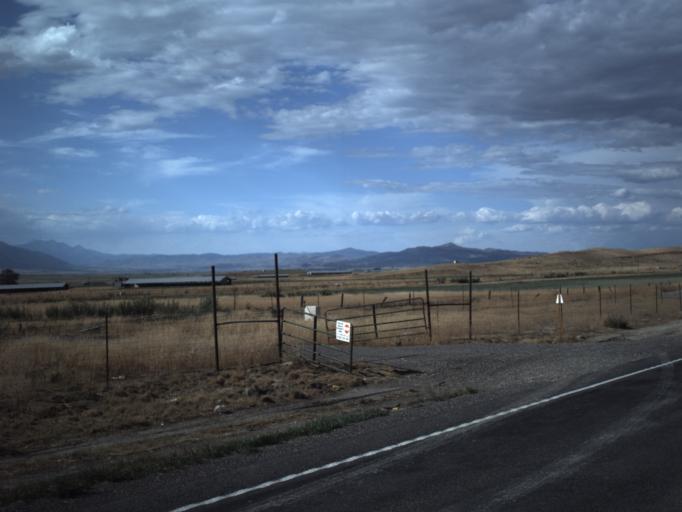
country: US
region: Utah
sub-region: Sanpete County
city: Ephraim
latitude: 39.3960
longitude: -111.5748
